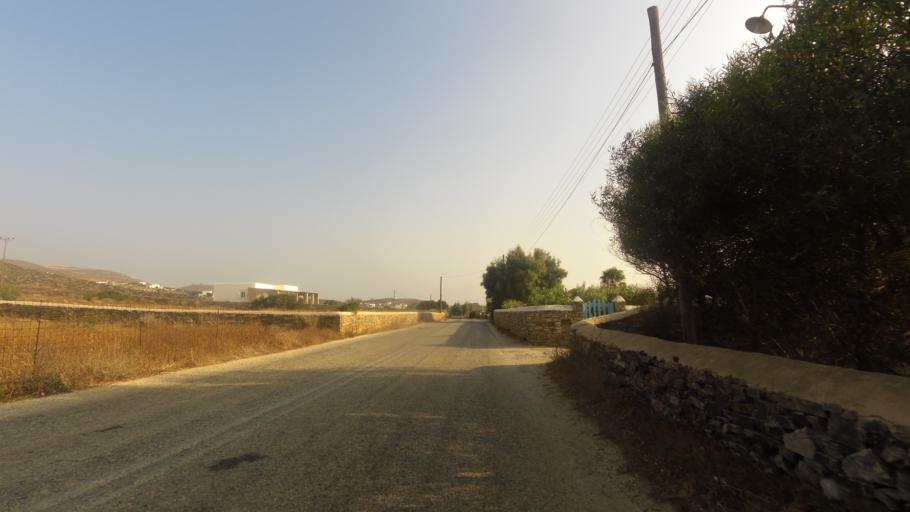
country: GR
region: South Aegean
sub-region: Nomos Kykladon
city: Antiparos
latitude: 37.0212
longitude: 25.0768
